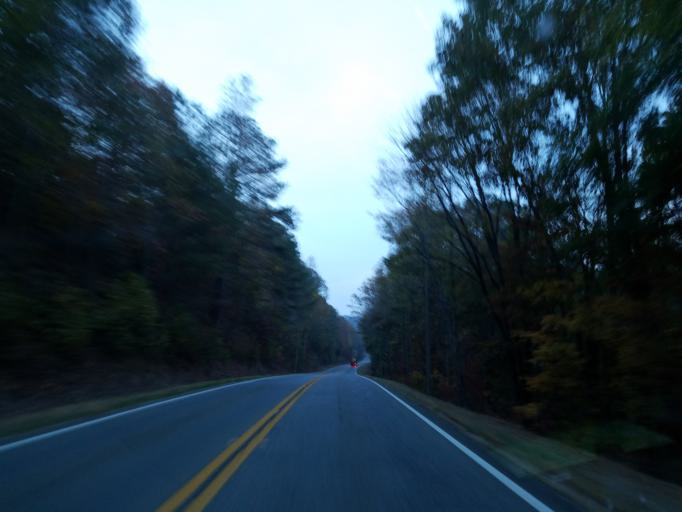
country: US
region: Georgia
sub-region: Pickens County
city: Jasper
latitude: 34.5385
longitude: -84.5779
